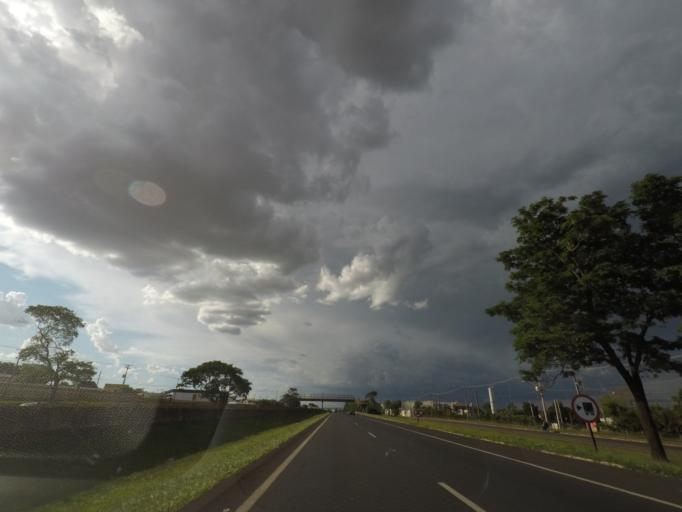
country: BR
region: Sao Paulo
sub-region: Ribeirao Preto
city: Ribeirao Preto
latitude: -21.1299
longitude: -47.7678
